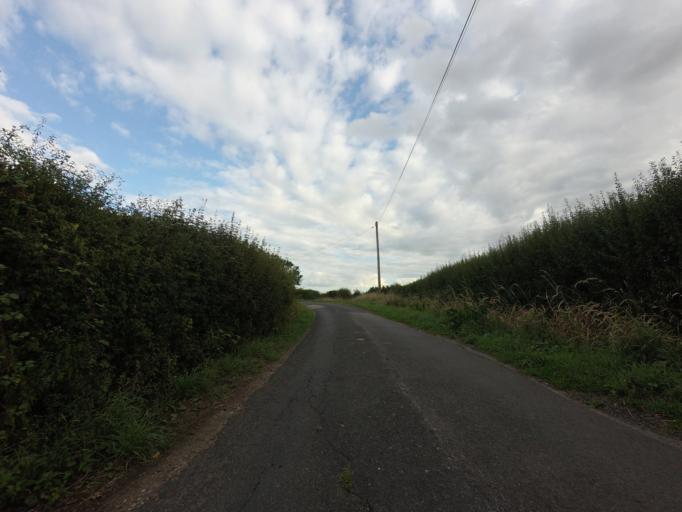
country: GB
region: England
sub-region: Kent
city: Staplehurst
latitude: 51.2062
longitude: 0.5395
